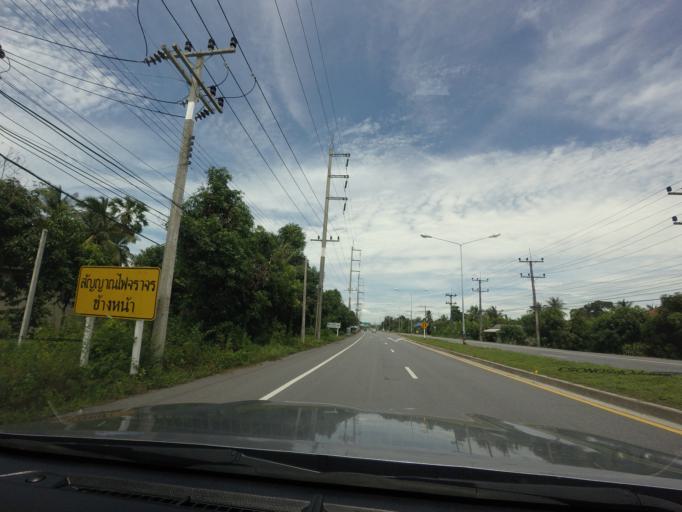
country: TH
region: Songkhla
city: Krasae Sin
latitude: 7.6062
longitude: 100.3997
